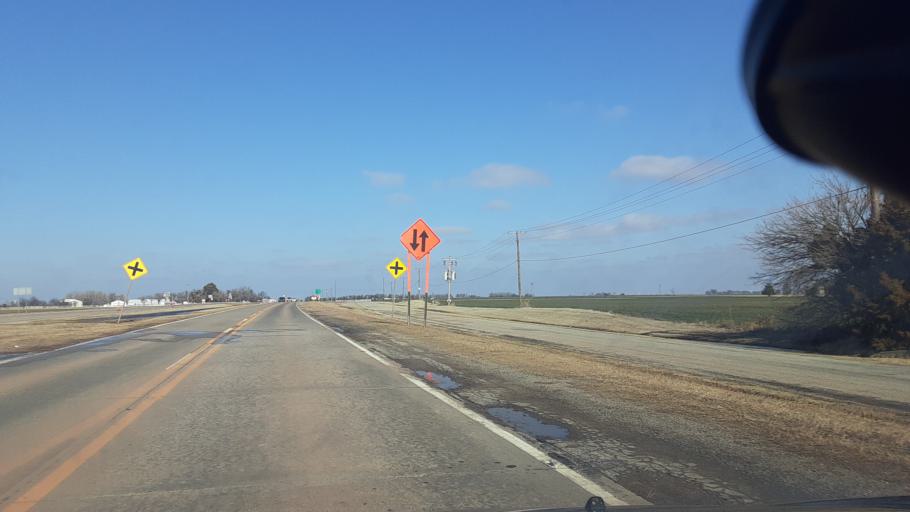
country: US
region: Oklahoma
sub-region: Garfield County
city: Enid
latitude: 36.4596
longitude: -97.8729
